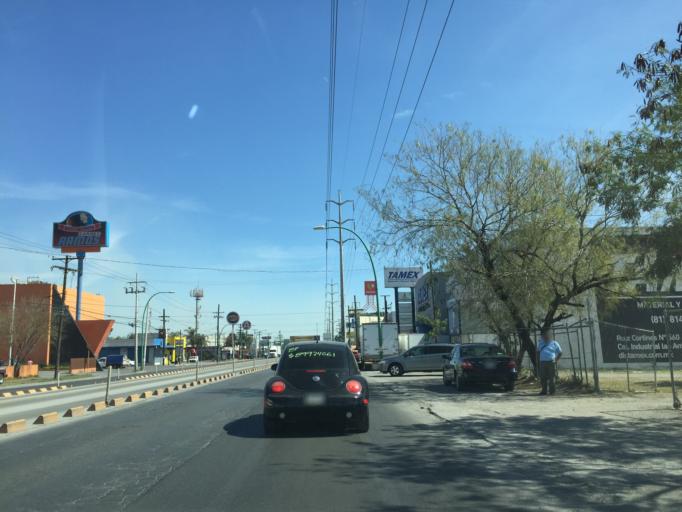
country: MX
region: Nuevo Leon
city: Guadalupe
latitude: 25.7029
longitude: -100.2422
